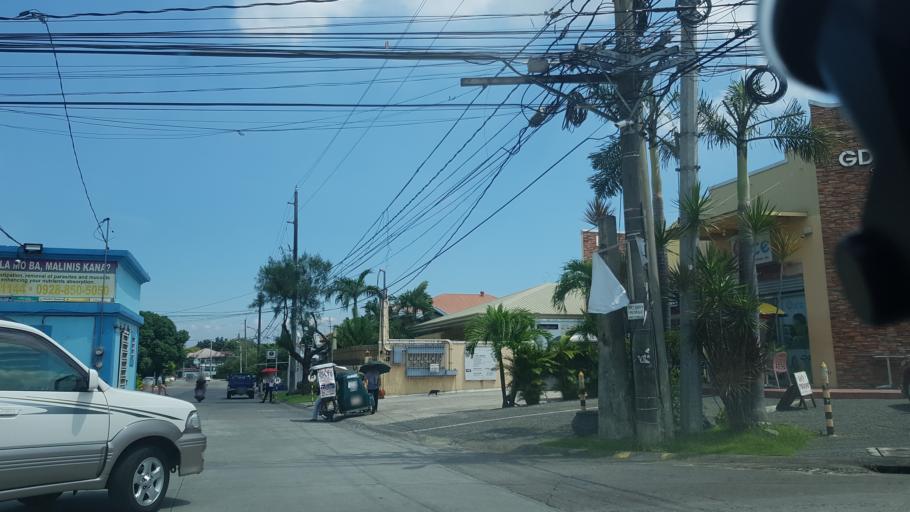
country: PH
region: Calabarzon
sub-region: Province of Rizal
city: Las Pinas
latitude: 14.4305
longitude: 120.9897
